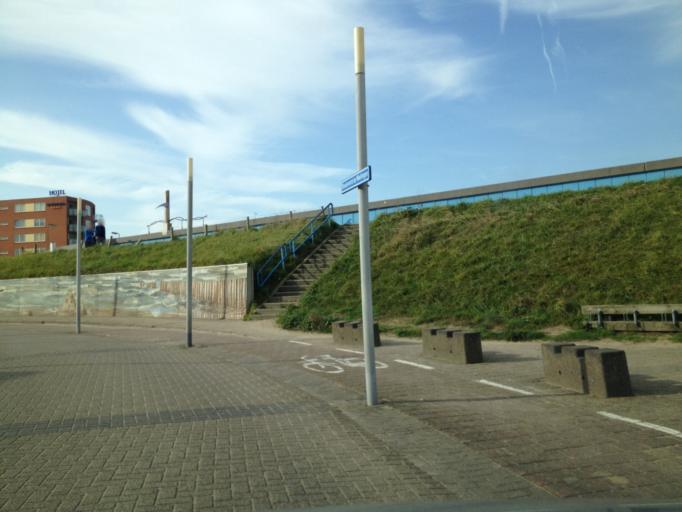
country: NL
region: Zeeland
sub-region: Gemeente Sluis
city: Sluis
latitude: 51.3774
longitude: 3.3831
